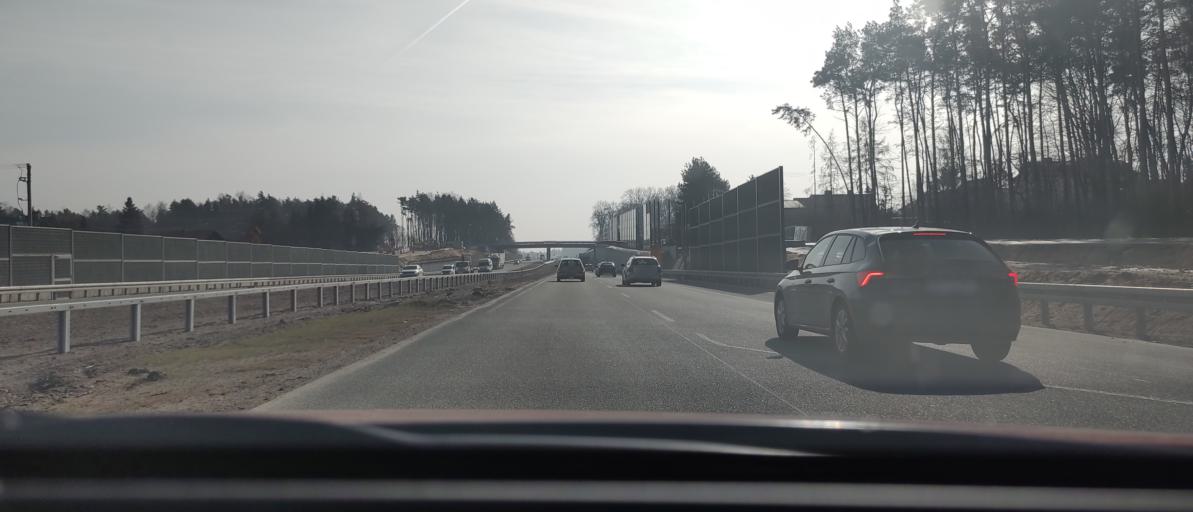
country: PL
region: Masovian Voivodeship
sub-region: Powiat grojecki
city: Grojec
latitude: 51.9111
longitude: 20.8559
